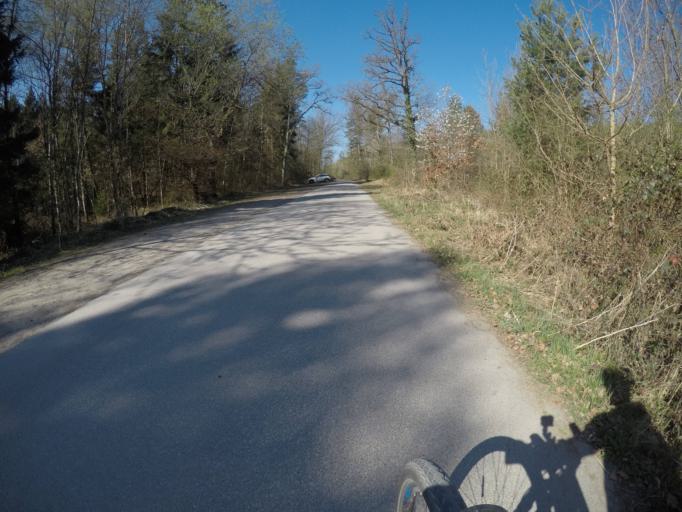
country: DE
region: Baden-Wuerttemberg
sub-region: Regierungsbezirk Stuttgart
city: Hildrizhausen
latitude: 48.5619
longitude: 8.9862
